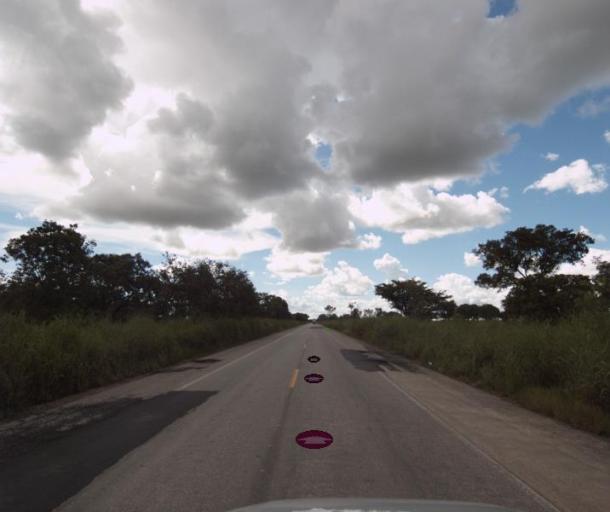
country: BR
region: Goias
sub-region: Porangatu
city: Porangatu
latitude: -13.5194
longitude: -49.1182
